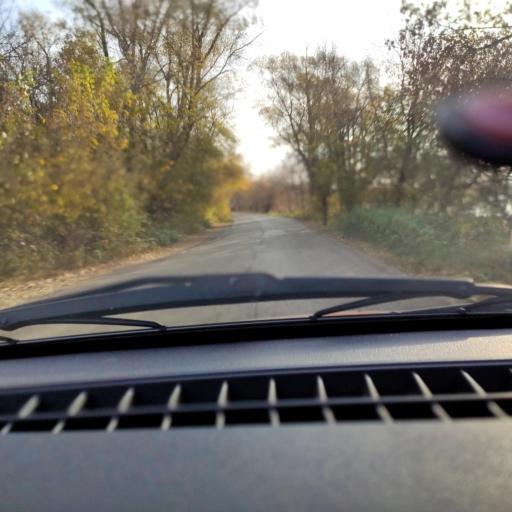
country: RU
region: Bashkortostan
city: Ufa
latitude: 54.7851
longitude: 56.1639
